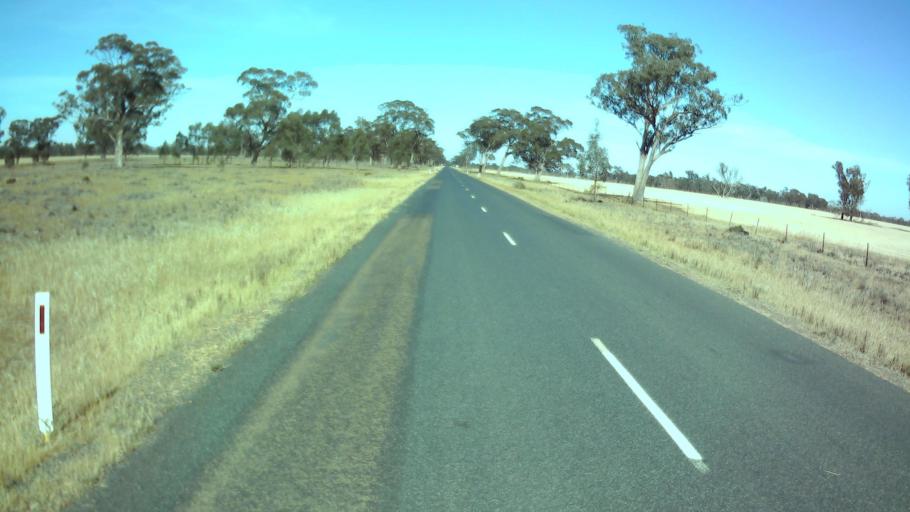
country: AU
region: New South Wales
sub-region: Weddin
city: Grenfell
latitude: -34.1364
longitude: 147.7693
